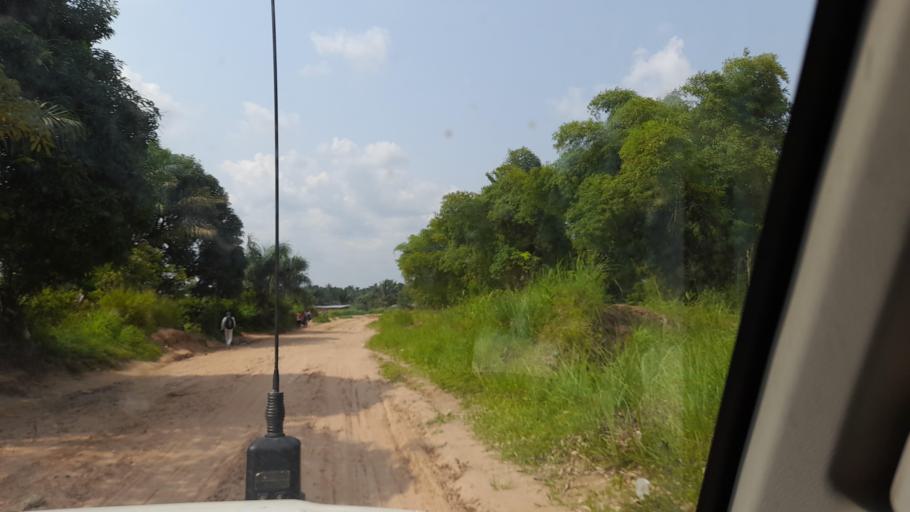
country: CD
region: Kasai-Occidental
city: Kananga
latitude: -5.9103
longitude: 22.4757
